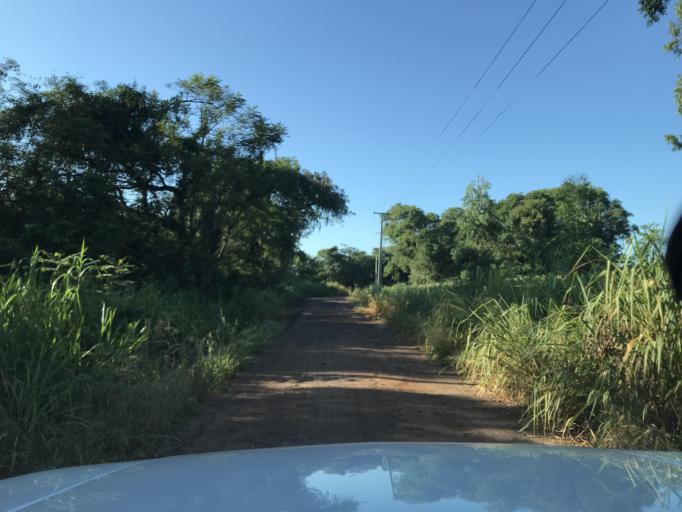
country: BR
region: Parana
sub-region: Palotina
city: Palotina
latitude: -24.2209
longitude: -53.7483
